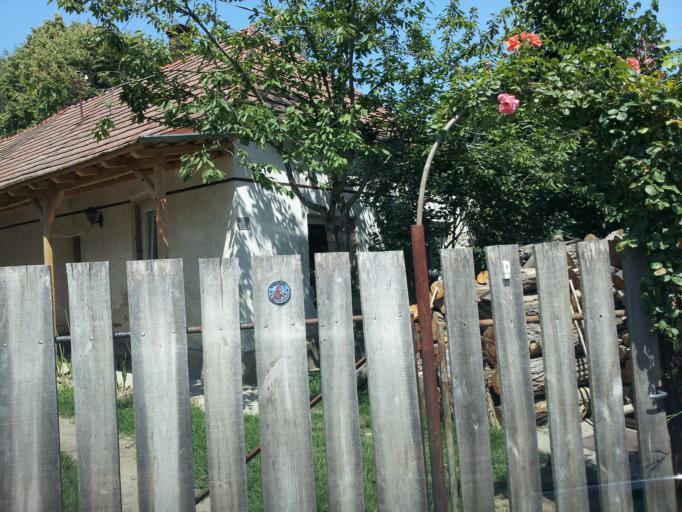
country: HU
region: Zala
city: Zalaegerszeg
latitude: 46.8517
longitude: 16.9337
